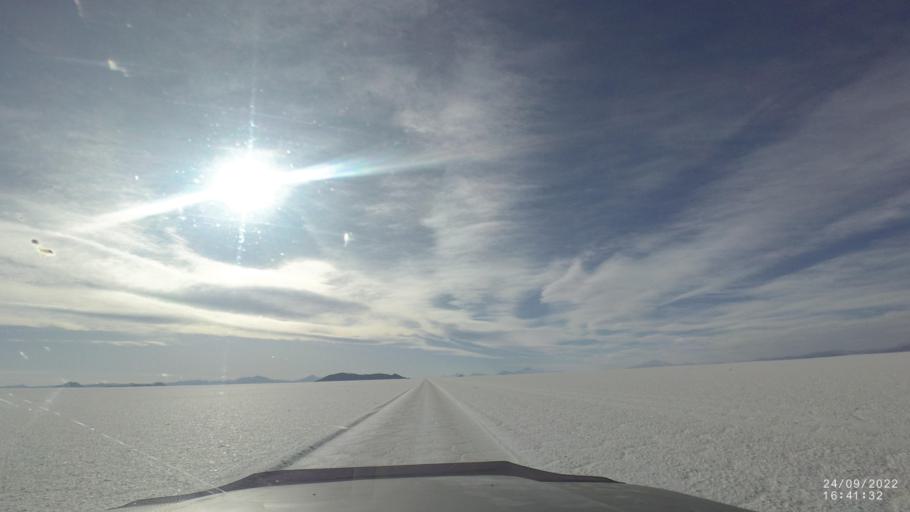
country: BO
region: Potosi
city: Colchani
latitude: -20.1842
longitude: -67.7169
